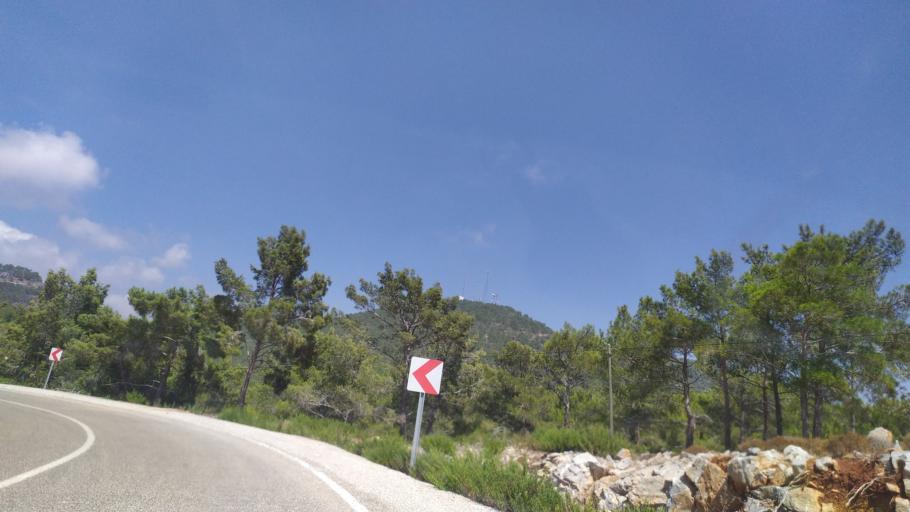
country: TR
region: Mersin
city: Aydincik
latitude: 36.1504
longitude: 33.3929
